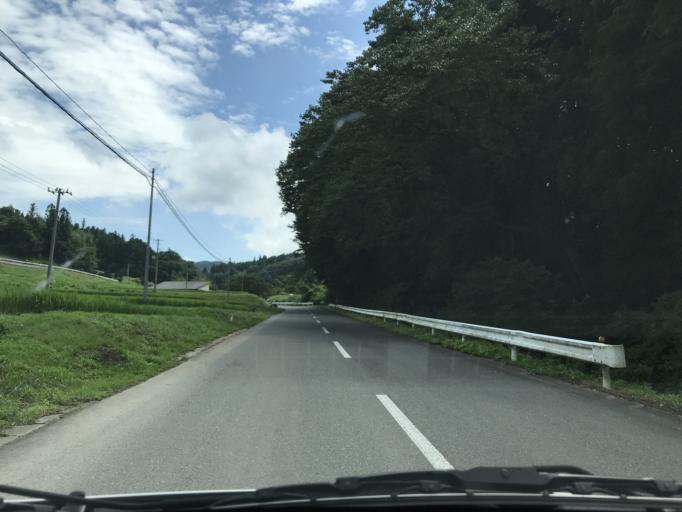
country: JP
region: Iwate
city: Mizusawa
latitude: 39.0597
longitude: 141.3965
